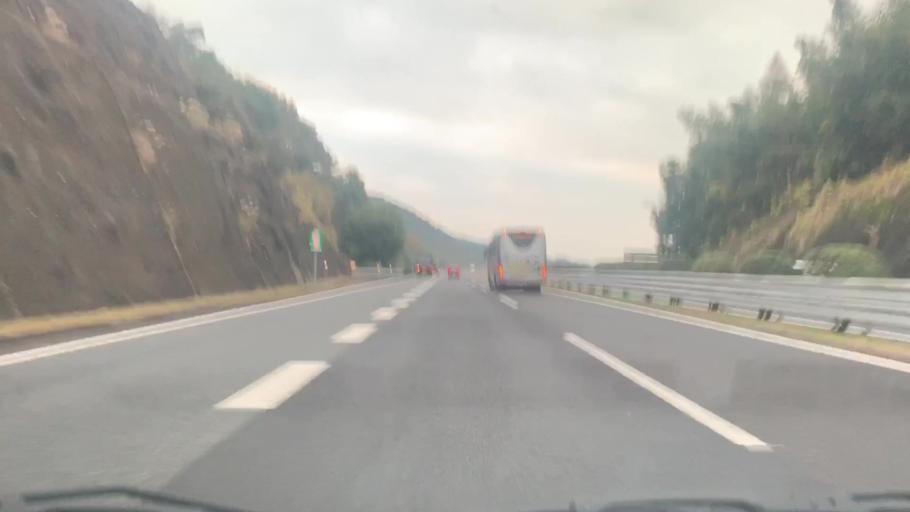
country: JP
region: Nagasaki
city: Omura
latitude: 32.9927
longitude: 129.9539
